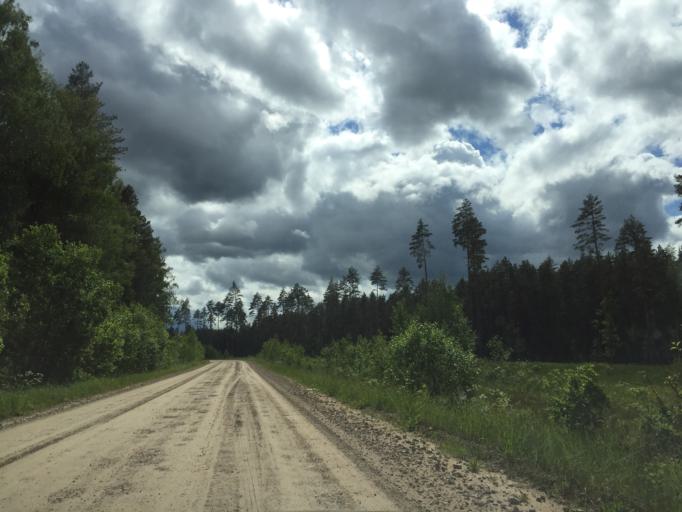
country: LV
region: Vecumnieki
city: Vecumnieki
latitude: 56.4913
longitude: 24.4088
